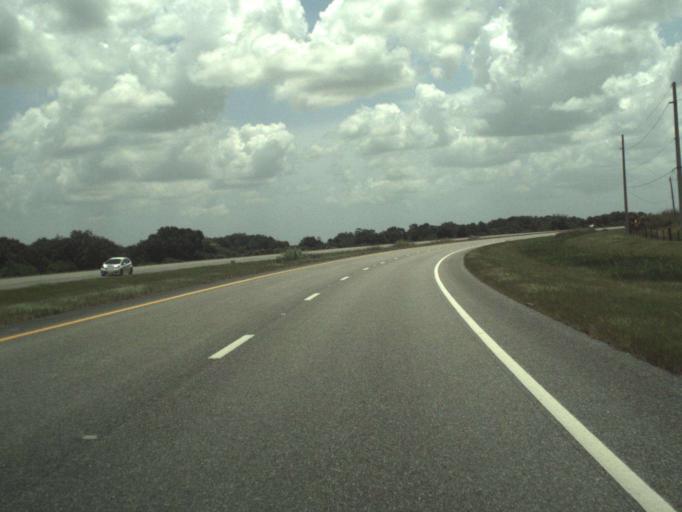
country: US
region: Florida
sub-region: Saint Lucie County
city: Fort Pierce South
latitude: 27.3756
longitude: -80.5714
